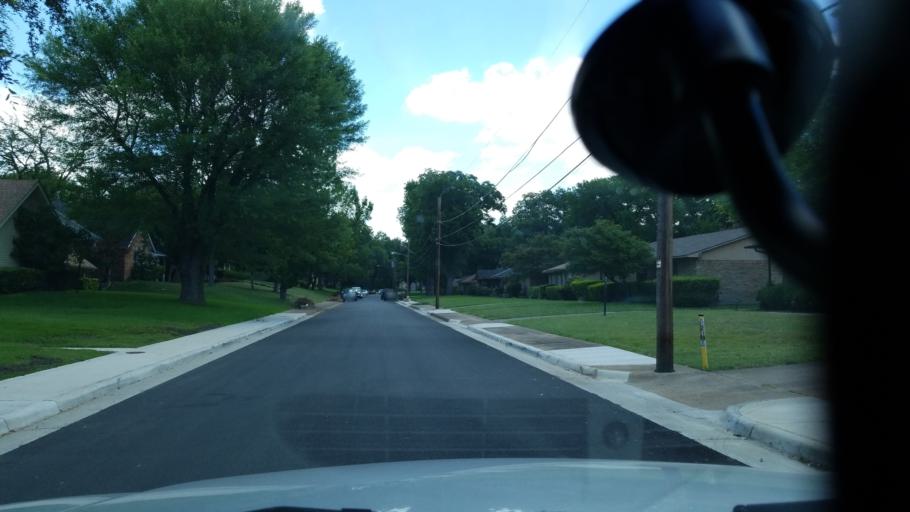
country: US
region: Texas
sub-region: Dallas County
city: Duncanville
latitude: 32.6673
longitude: -96.8627
